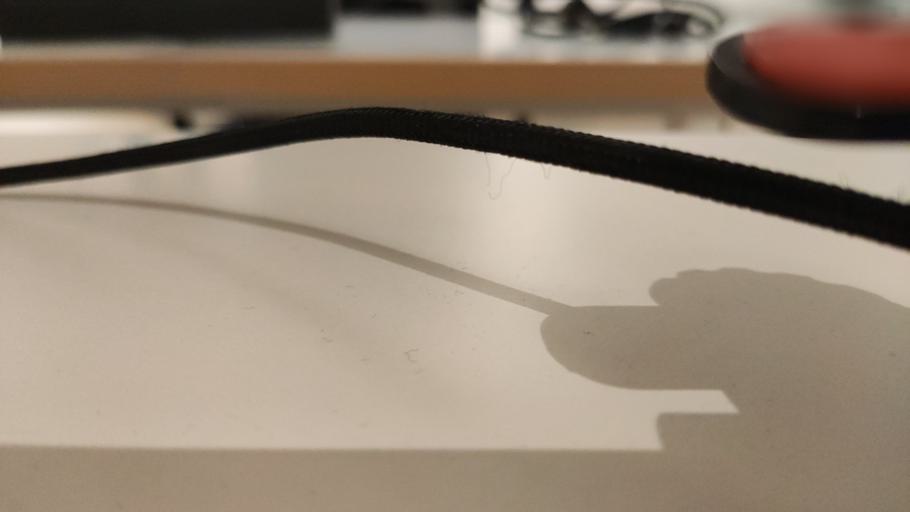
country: RU
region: Kaluga
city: Belousovo
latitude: 55.1467
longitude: 36.7586
